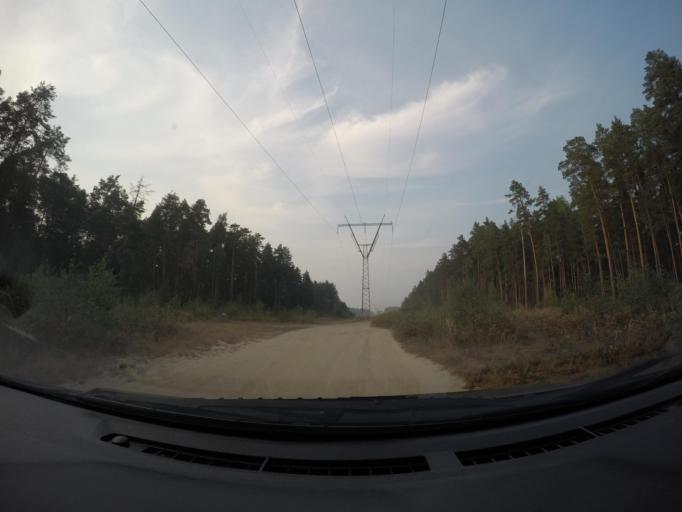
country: RU
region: Moskovskaya
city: Imeni Tsyurupy
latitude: 55.5010
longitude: 38.6876
